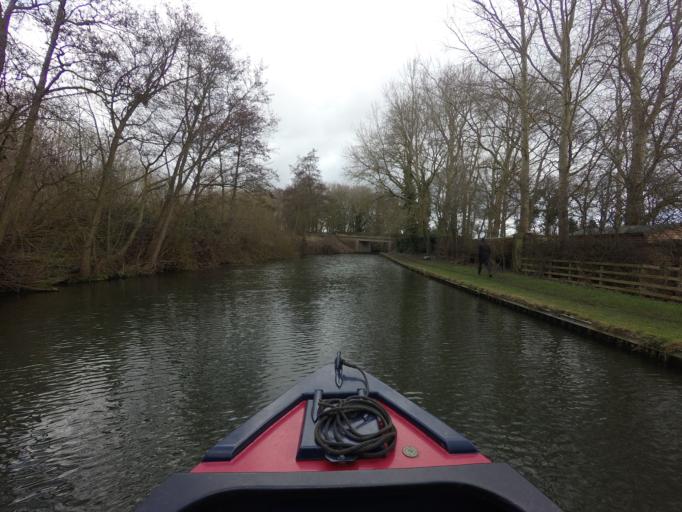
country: GB
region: England
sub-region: Northamptonshire
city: Long Buckby
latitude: 52.2468
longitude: -1.0848
